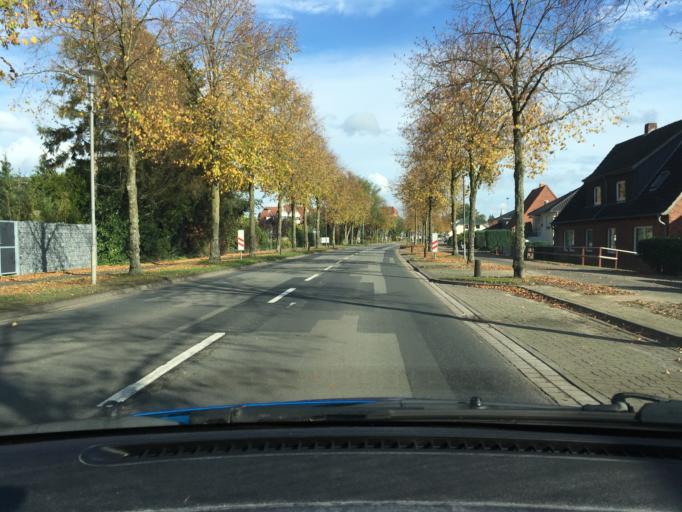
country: DE
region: Lower Saxony
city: Wistedt
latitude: 53.2792
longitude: 9.6963
